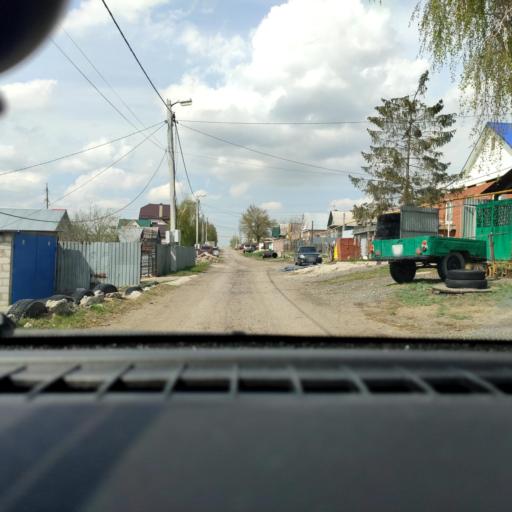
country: RU
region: Samara
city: Zhigulevsk
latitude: 53.4842
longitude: 49.5364
